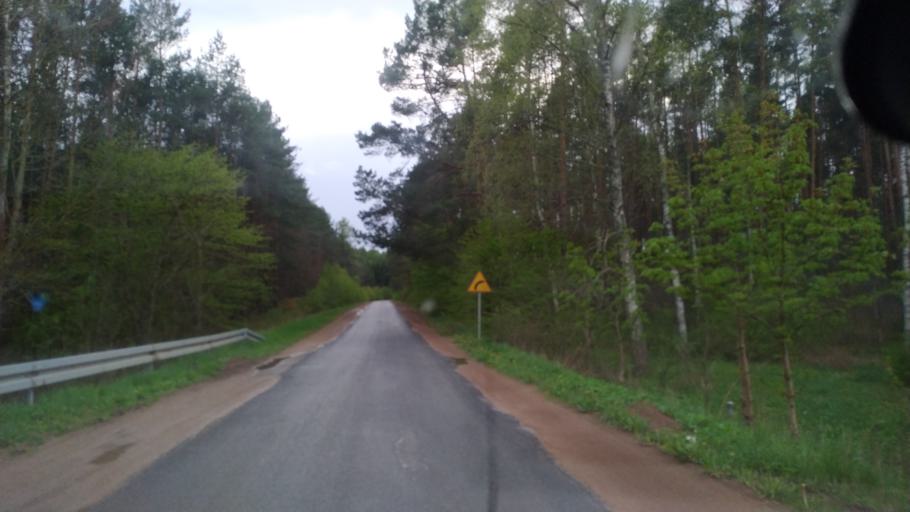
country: PL
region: Pomeranian Voivodeship
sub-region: Powiat starogardzki
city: Osiek
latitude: 53.6958
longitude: 18.5559
